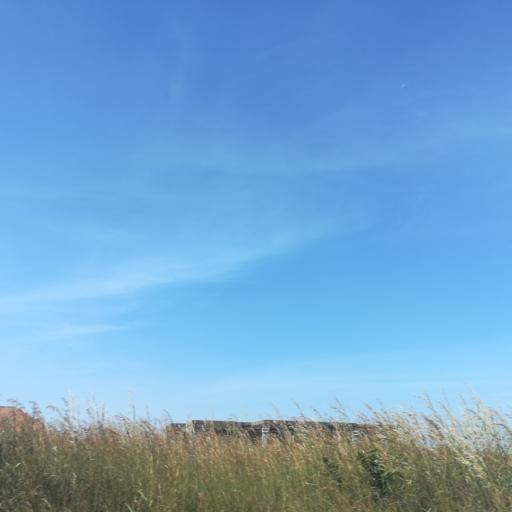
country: NG
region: Plateau
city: Bukuru
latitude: 9.7661
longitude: 8.8879
